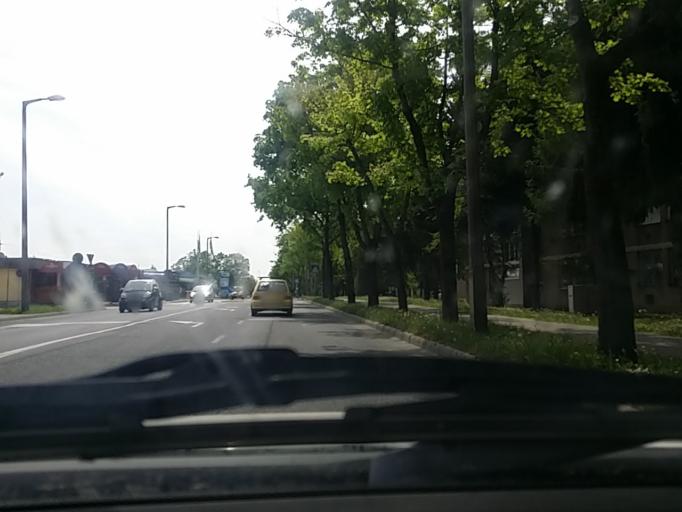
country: HU
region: Zala
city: Nagykanizsa
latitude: 46.4574
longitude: 17.0096
